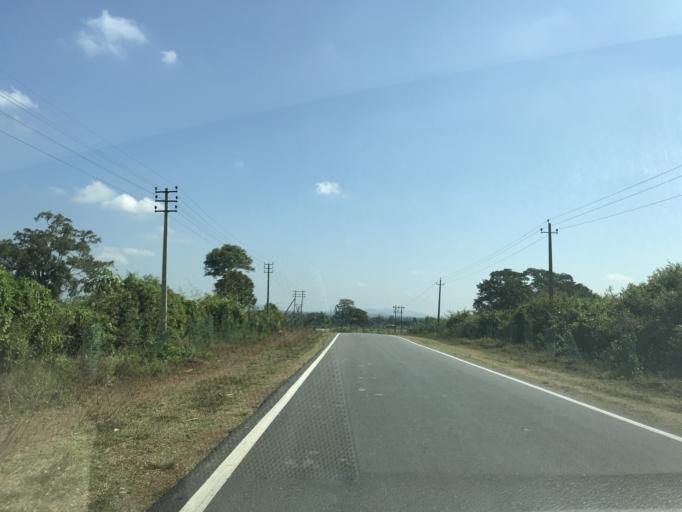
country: IN
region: Karnataka
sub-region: Mysore
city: Heggadadevankote
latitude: 12.0155
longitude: 76.2747
